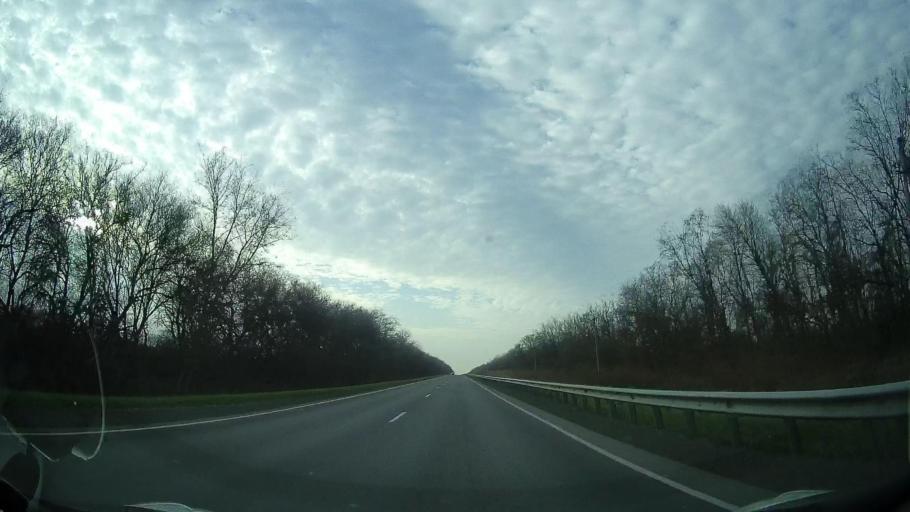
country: RU
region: Rostov
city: Bagayevskaya
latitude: 47.0928
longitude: 40.3778
